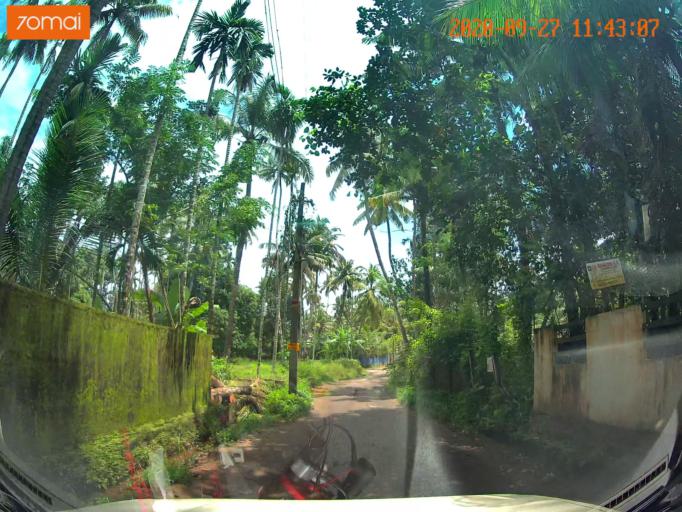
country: IN
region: Kerala
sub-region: Thrissur District
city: Thanniyam
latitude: 10.4732
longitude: 76.1125
